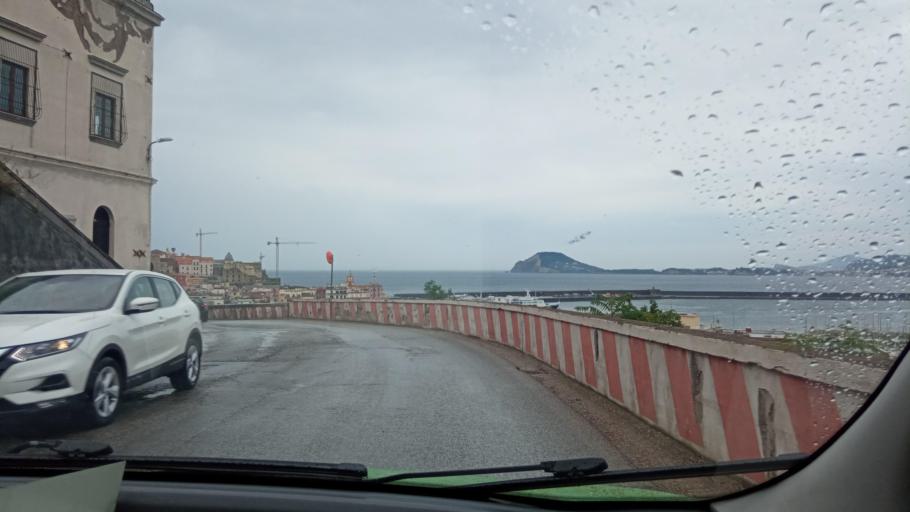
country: IT
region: Campania
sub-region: Provincia di Napoli
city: Pozzuoli
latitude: 40.8286
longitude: 14.1203
